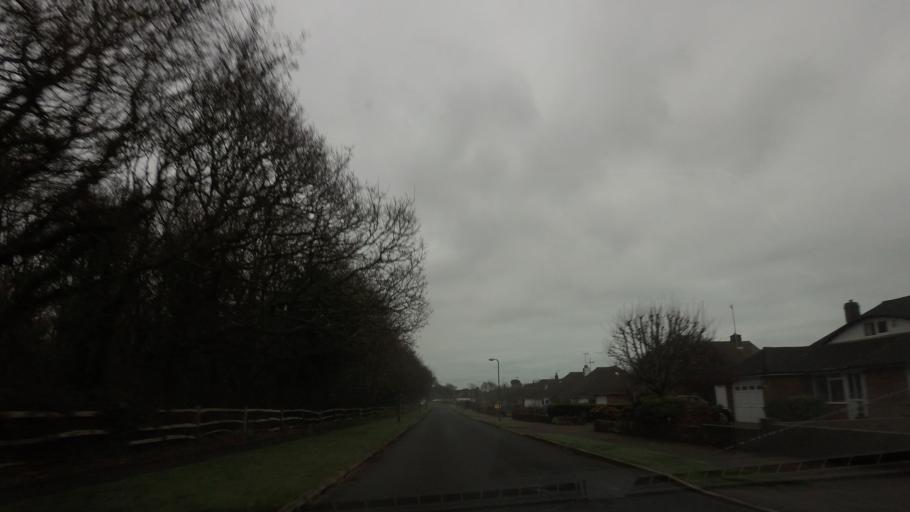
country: GB
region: England
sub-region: East Sussex
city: Bexhill-on-Sea
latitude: 50.8361
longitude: 0.4359
